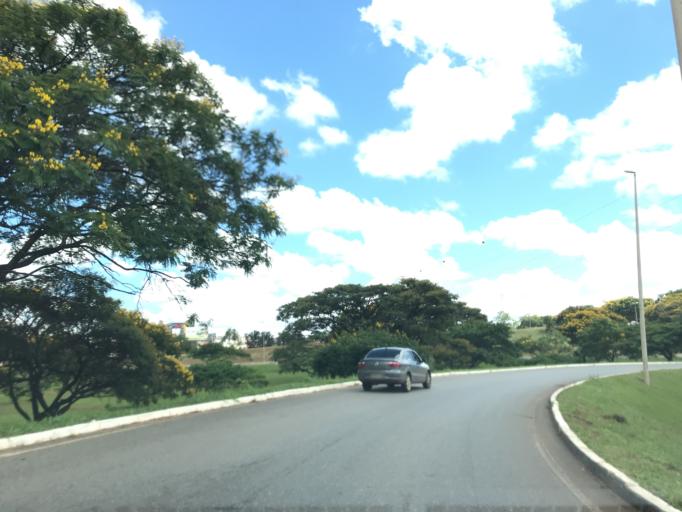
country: BR
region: Federal District
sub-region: Brasilia
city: Brasilia
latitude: -15.8094
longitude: -47.9494
